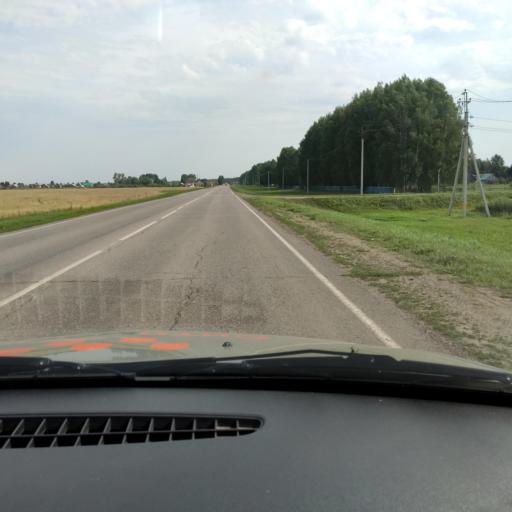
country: RU
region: Bashkortostan
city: Krasnaya Gorka
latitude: 55.0841
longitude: 56.6082
